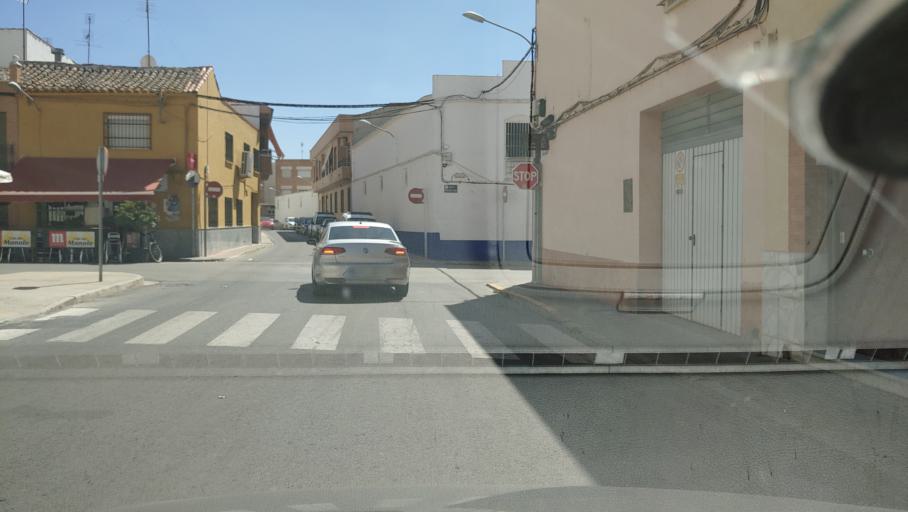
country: ES
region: Castille-La Mancha
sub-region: Provincia de Ciudad Real
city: Valdepenas
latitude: 38.7649
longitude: -3.3832
